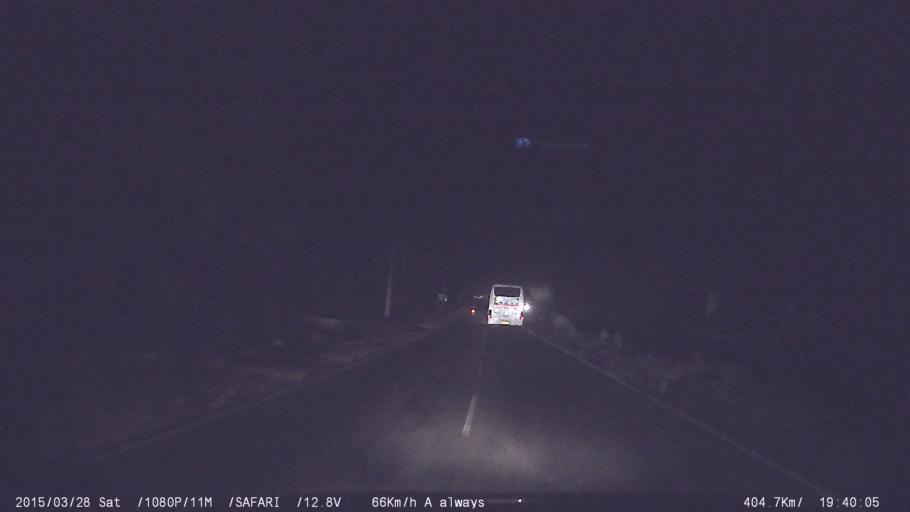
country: IN
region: Karnataka
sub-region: Mandya
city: Shrirangapattana
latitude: 12.4496
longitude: 76.7373
